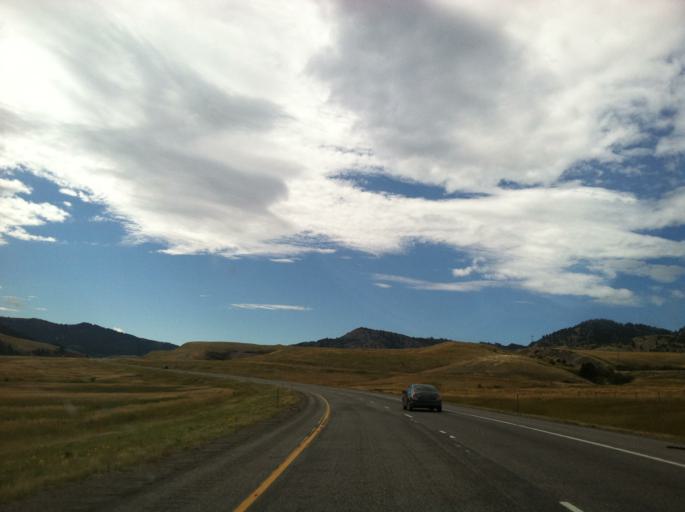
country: US
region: Montana
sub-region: Park County
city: Livingston
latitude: 45.6639
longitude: -110.7175
